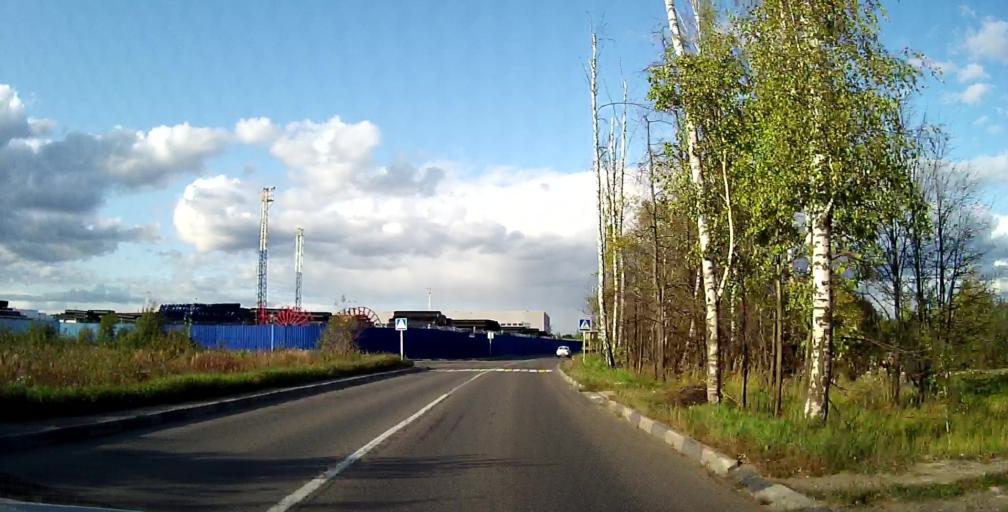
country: RU
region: Moskovskaya
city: Klimovsk
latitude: 55.3665
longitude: 37.5668
